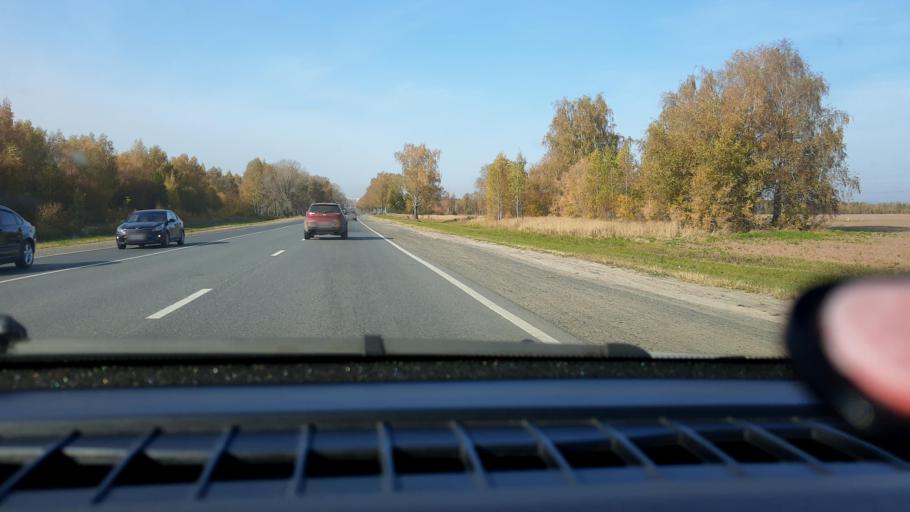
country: RU
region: Nizjnij Novgorod
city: Kstovo
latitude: 56.1332
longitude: 44.2472
